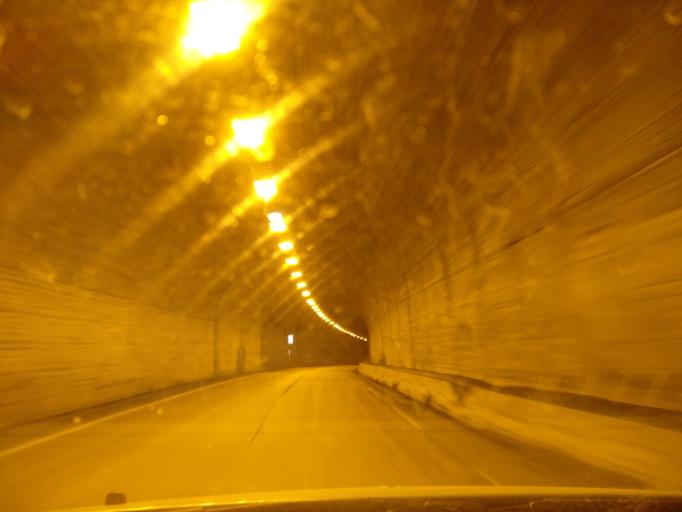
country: NO
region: Hordaland
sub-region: Odda
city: Odda
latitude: 59.8496
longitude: 6.9469
